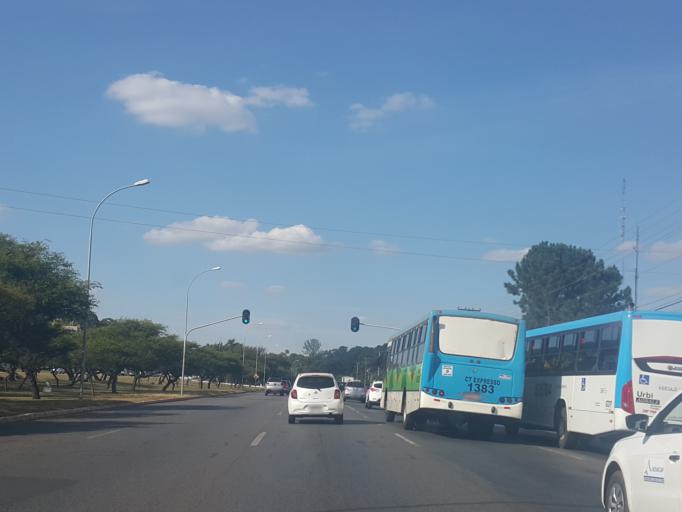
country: BR
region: Federal District
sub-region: Brasilia
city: Brasilia
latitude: -15.8086
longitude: -47.9329
